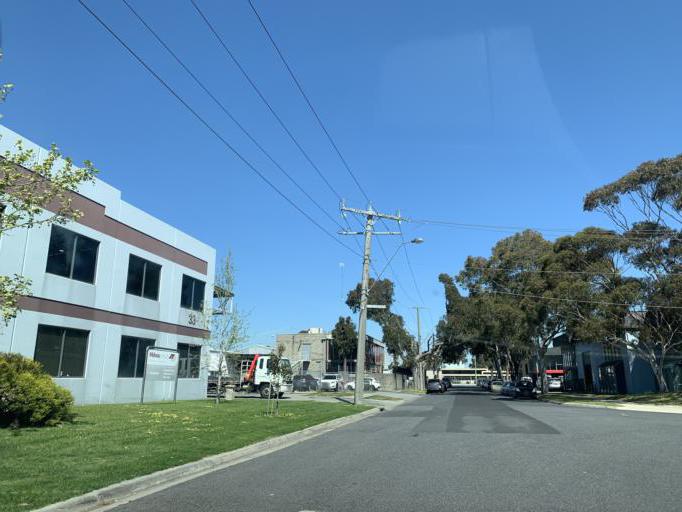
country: AU
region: Victoria
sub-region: Greater Dandenong
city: Dandenong
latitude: -38.0124
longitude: 145.2099
